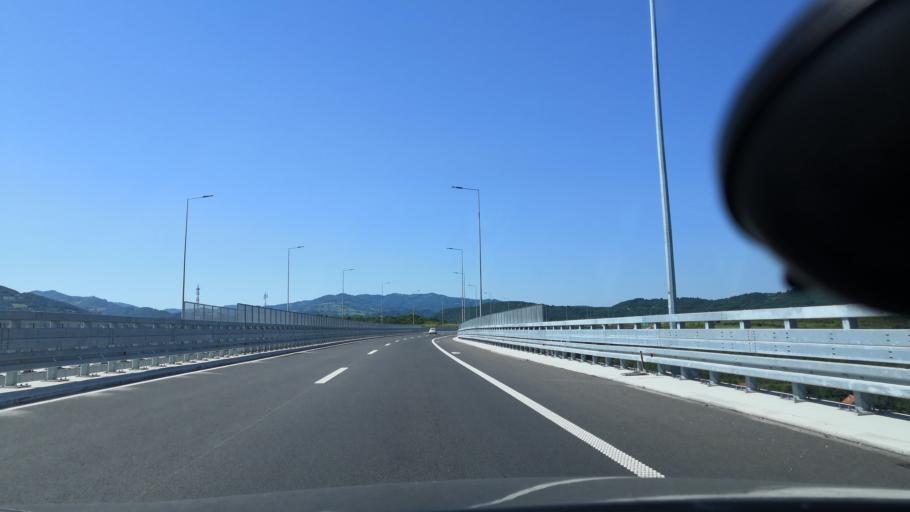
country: RS
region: Central Serbia
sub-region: Pcinjski Okrug
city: Vladicin Han
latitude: 42.7078
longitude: 22.0729
